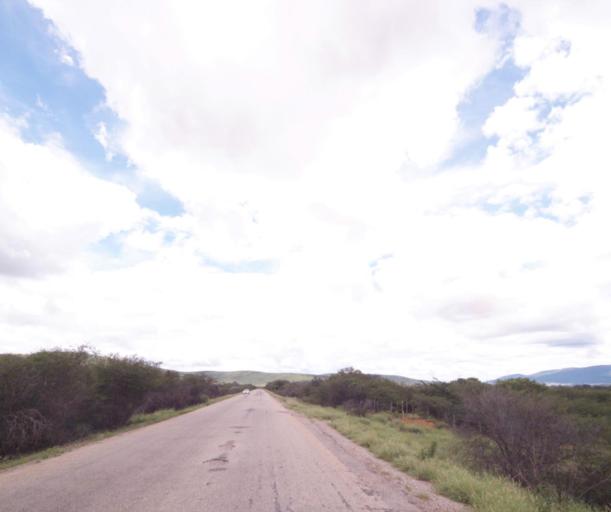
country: BR
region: Bahia
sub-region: Brumado
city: Brumado
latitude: -14.1822
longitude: -41.5703
